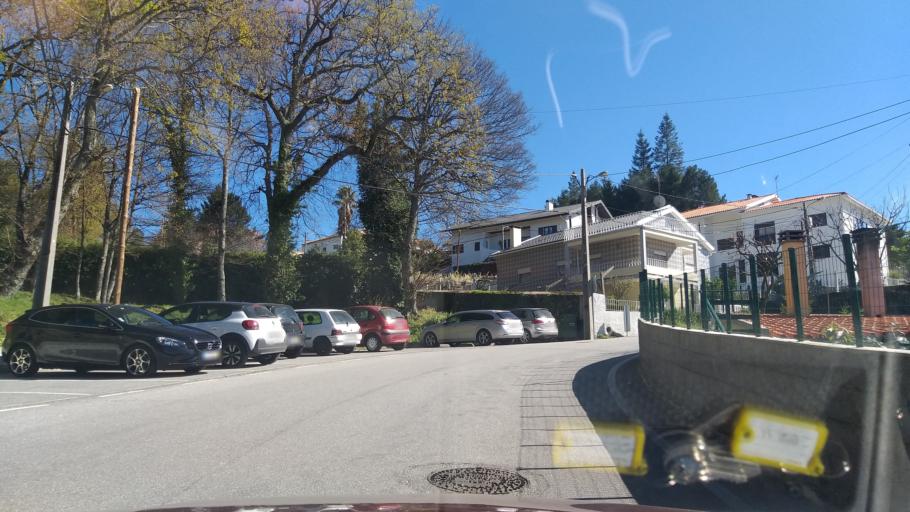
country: PT
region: Guarda
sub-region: Manteigas
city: Manteigas
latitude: 40.4925
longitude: -7.5888
